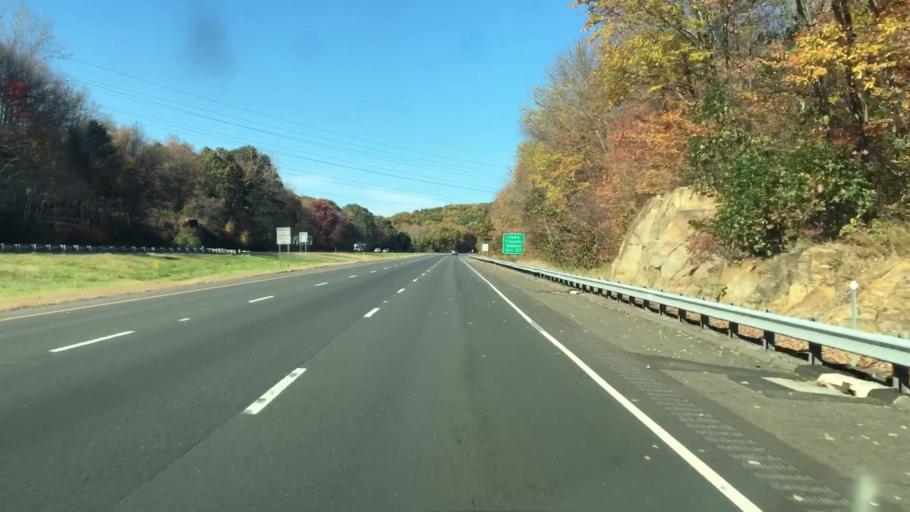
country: US
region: Connecticut
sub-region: Litchfield County
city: Oakville
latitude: 41.5944
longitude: -73.0630
